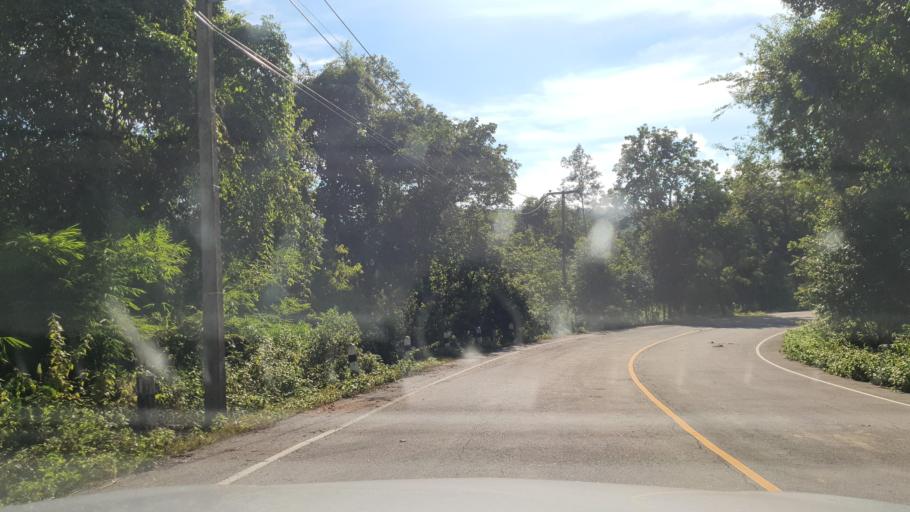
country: TH
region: Chiang Mai
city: Mae On
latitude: 18.7937
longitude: 99.3038
